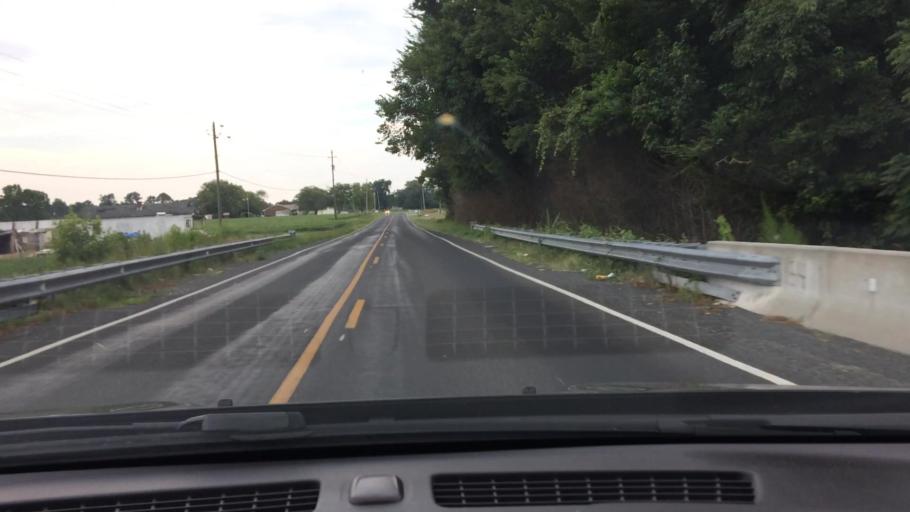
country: US
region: North Carolina
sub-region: Pitt County
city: Ayden
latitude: 35.4503
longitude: -77.4109
